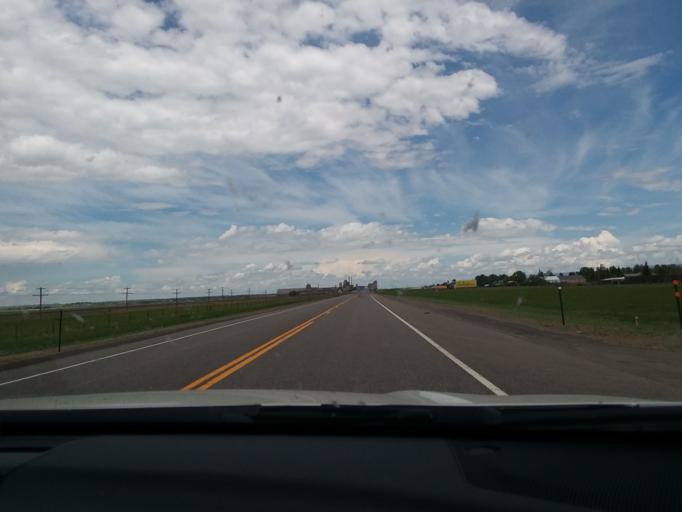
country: US
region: Wyoming
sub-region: Albany County
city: Laramie
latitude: 41.2487
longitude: -105.6017
